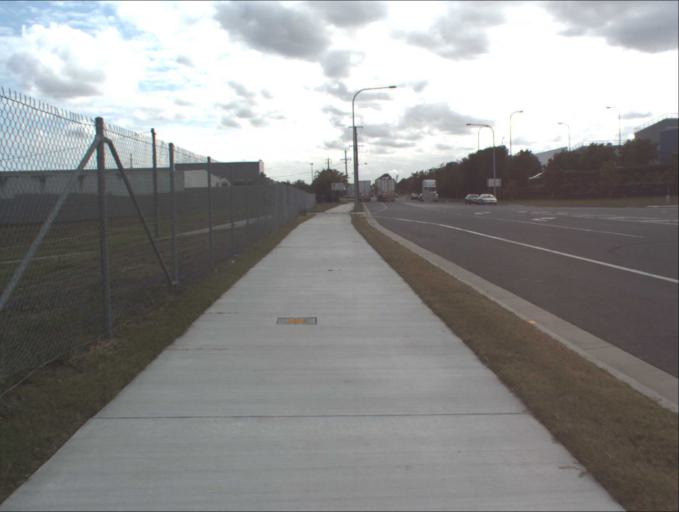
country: AU
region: Queensland
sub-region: Logan
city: Logan Reserve
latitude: -27.6876
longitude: 153.0696
